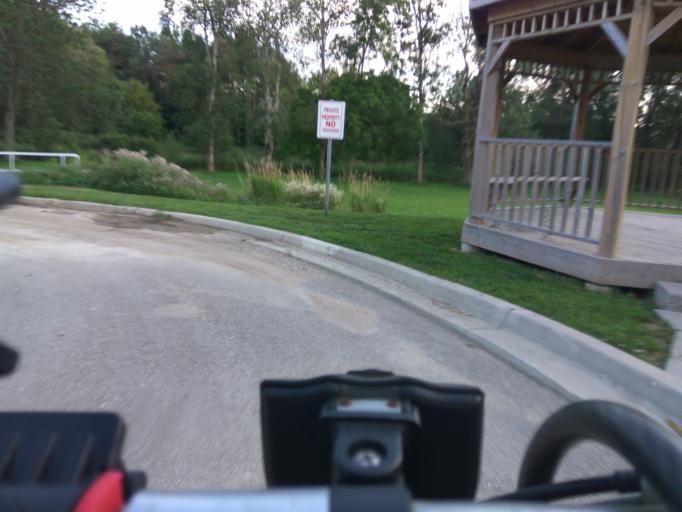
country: CA
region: Ontario
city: Stratford
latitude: 43.3860
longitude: -80.9613
